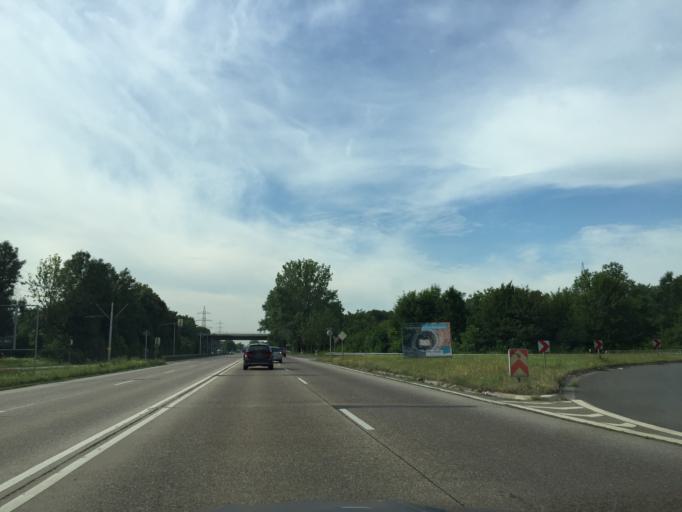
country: DE
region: Baden-Wuerttemberg
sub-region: Karlsruhe Region
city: Leimen
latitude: 49.3708
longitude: 8.6879
